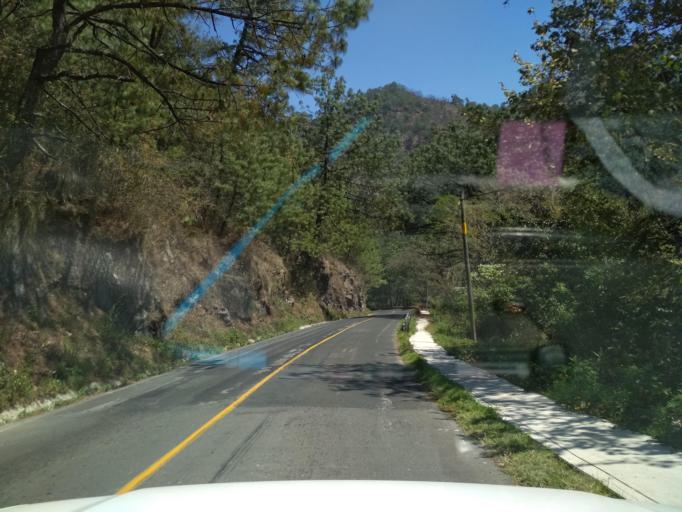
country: MX
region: Veracruz
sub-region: Tlilapan
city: Tonalixco
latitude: 18.7691
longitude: -97.0811
